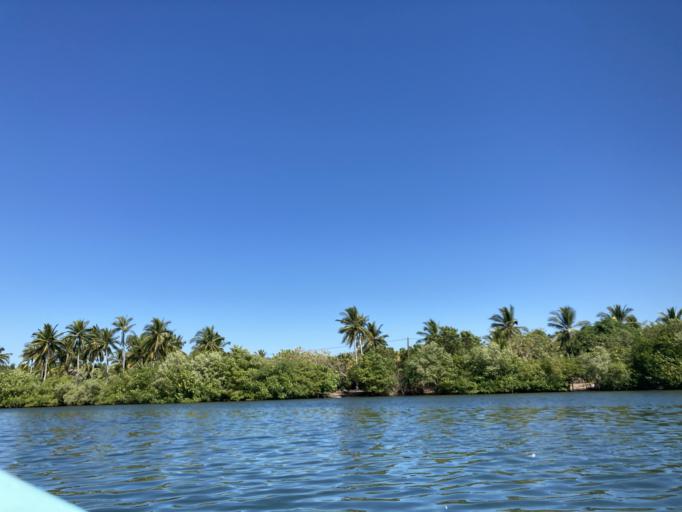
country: GT
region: Jutiapa
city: Pasaco
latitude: 13.8087
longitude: -90.2710
